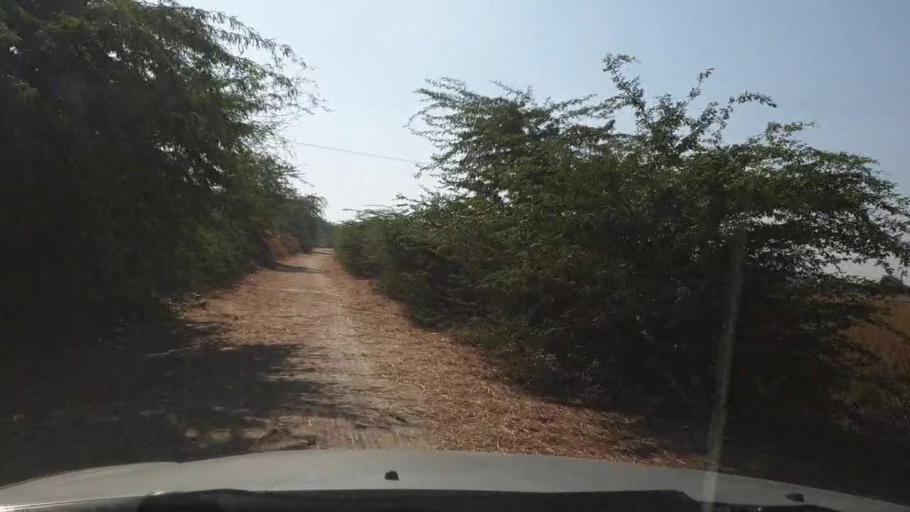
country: PK
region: Sindh
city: Kario
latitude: 24.8972
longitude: 68.5646
